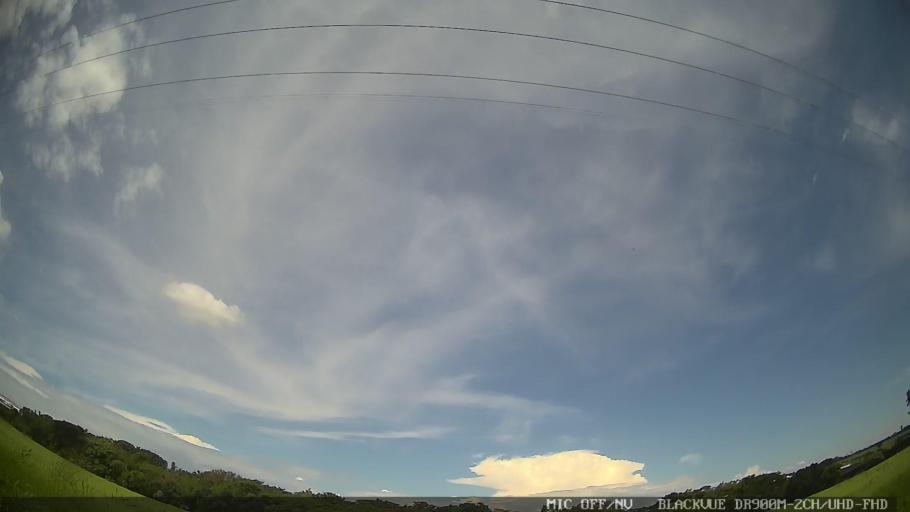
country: BR
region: Sao Paulo
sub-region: Artur Nogueira
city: Artur Nogueira
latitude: -22.6106
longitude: -47.0625
